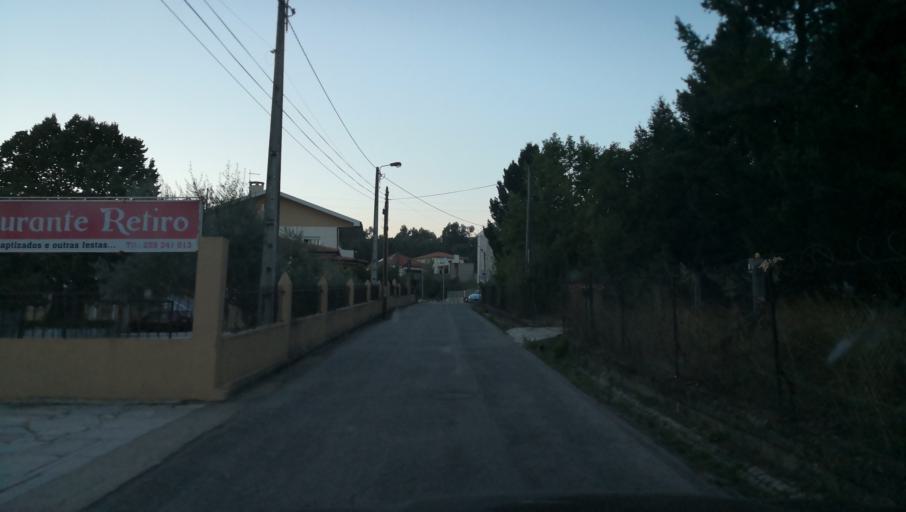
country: PT
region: Vila Real
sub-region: Vila Real
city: Vila Real
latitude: 41.3104
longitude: -7.7646
